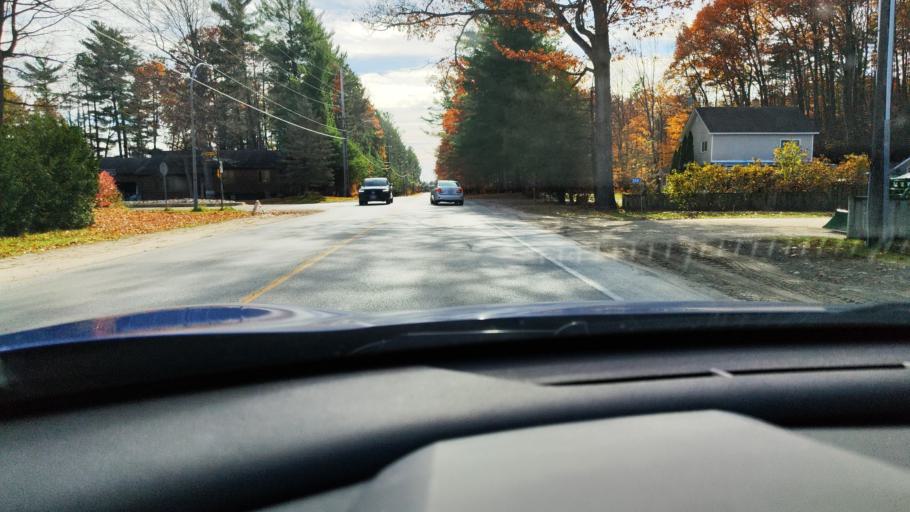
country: CA
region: Ontario
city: Wasaga Beach
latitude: 44.5173
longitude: -79.9950
